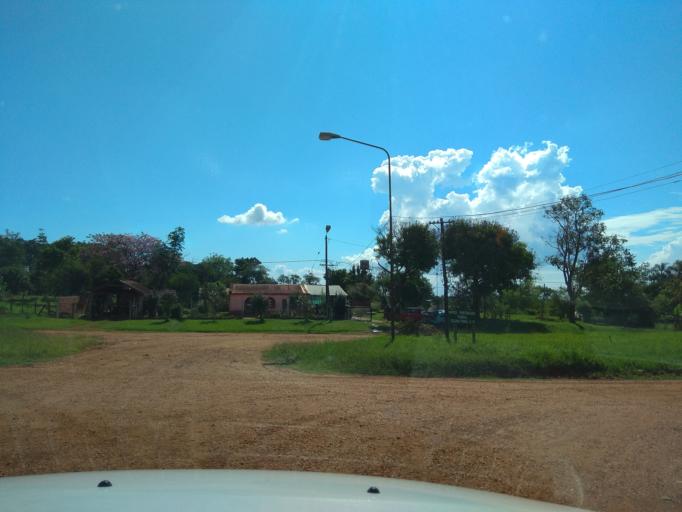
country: AR
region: Misiones
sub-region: Departamento de Candelaria
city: Candelaria
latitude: -27.4596
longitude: -55.7548
